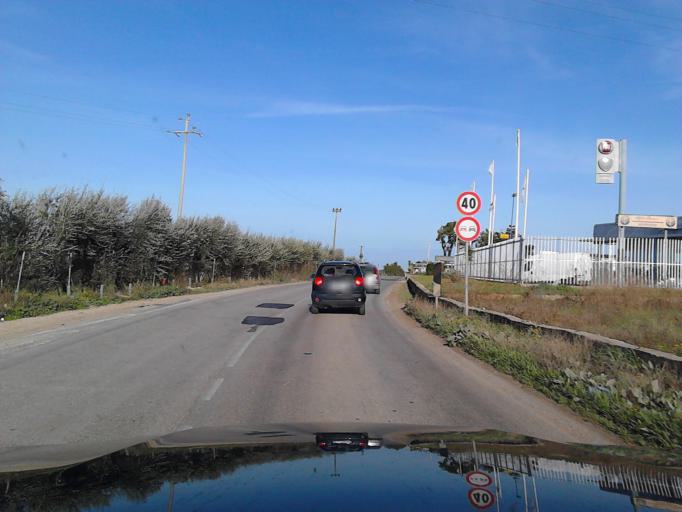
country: IT
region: Apulia
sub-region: Provincia di Bari
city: Noicattaro
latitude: 41.0160
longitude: 16.9644
